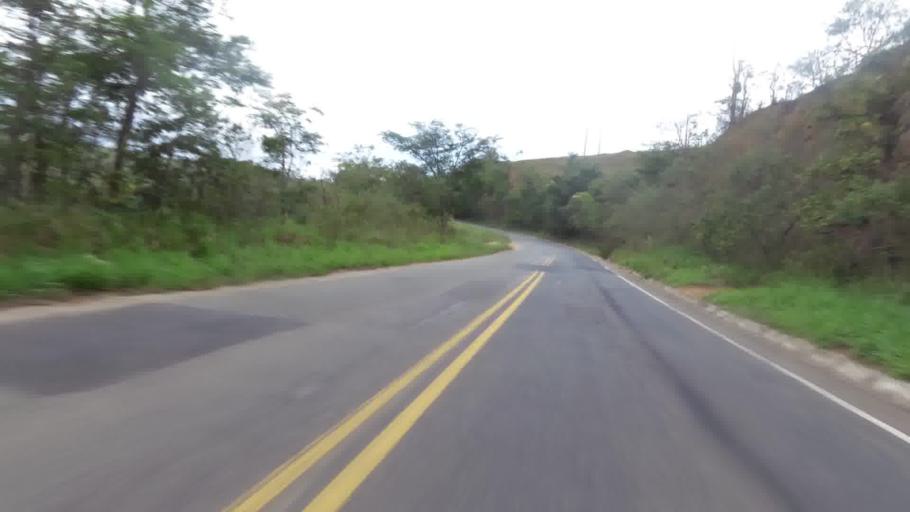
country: BR
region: Espirito Santo
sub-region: Alfredo Chaves
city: Alfredo Chaves
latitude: -20.6635
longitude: -40.7158
